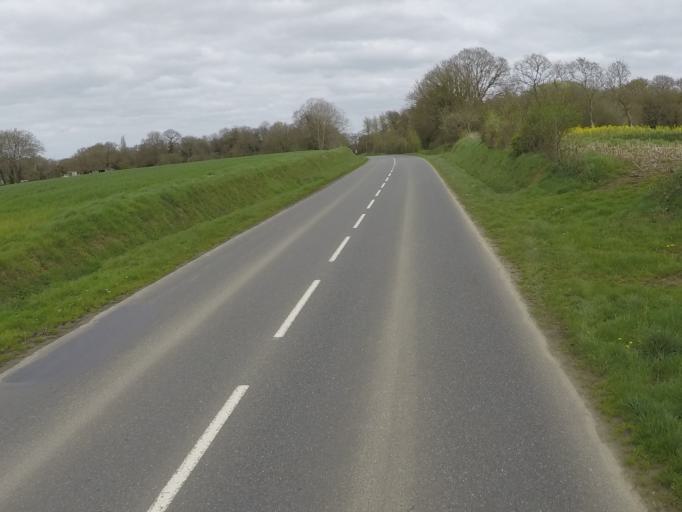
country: FR
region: Brittany
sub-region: Departement des Cotes-d'Armor
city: Pleguien
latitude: 48.6603
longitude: -2.9535
